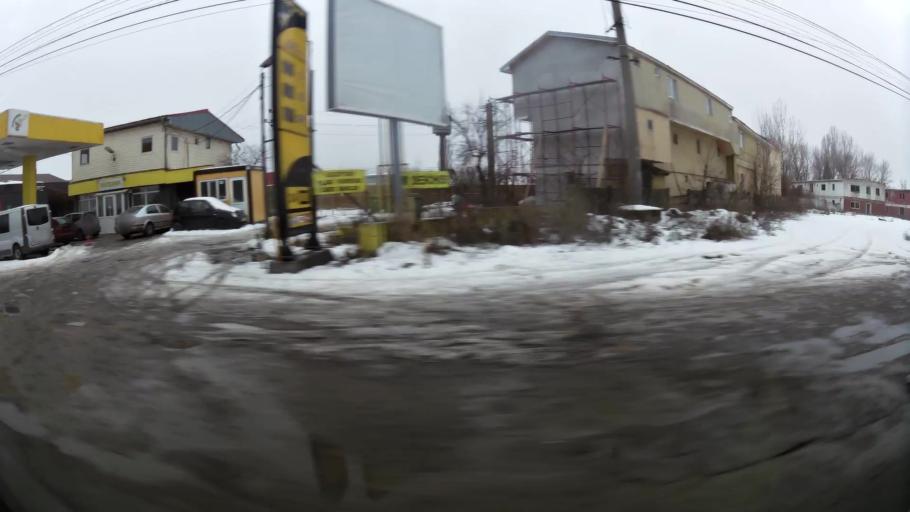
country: RO
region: Ilfov
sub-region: Comuna Bragadiru
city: Bragadiru
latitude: 44.3850
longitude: 25.9904
